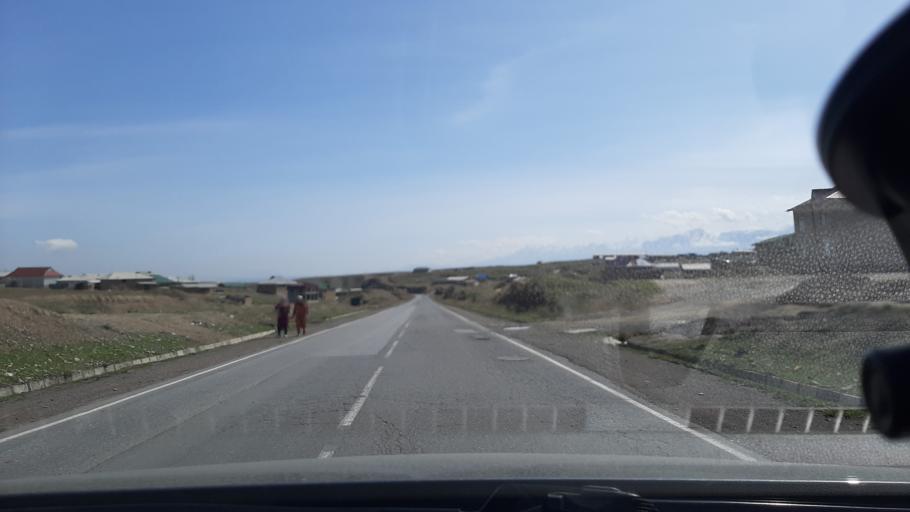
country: TJ
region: Viloyati Sughd
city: Shahriston
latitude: 39.7625
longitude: 68.8060
